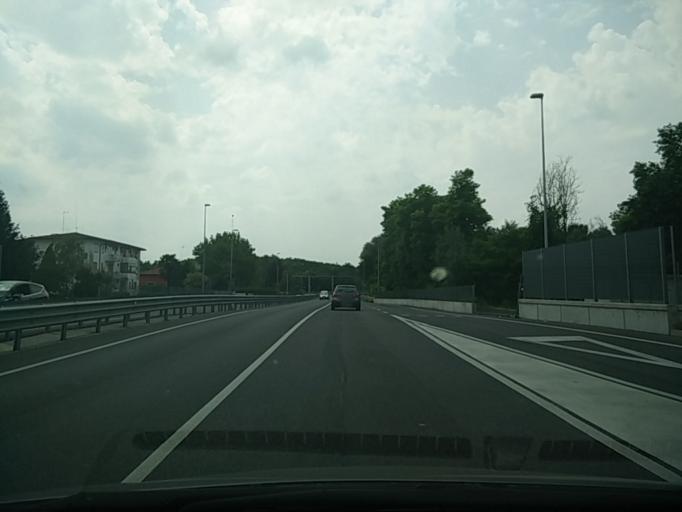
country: IT
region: Friuli Venezia Giulia
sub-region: Provincia di Pordenone
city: Fiume Veneto
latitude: 45.9448
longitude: 12.7062
